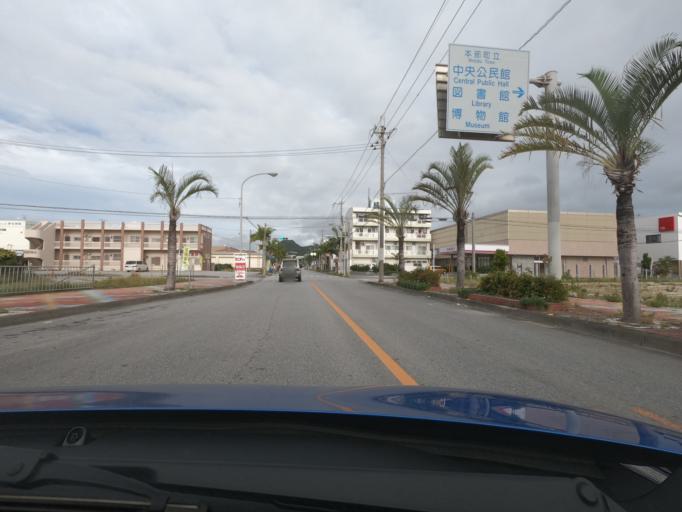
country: JP
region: Okinawa
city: Nago
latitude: 26.6564
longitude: 127.8839
